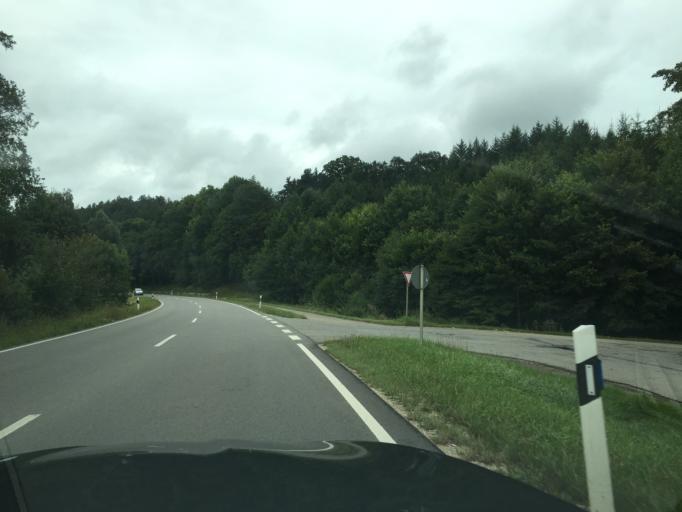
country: DE
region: Bavaria
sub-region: Swabia
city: Zusmarshausen
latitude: 48.4210
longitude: 10.6004
